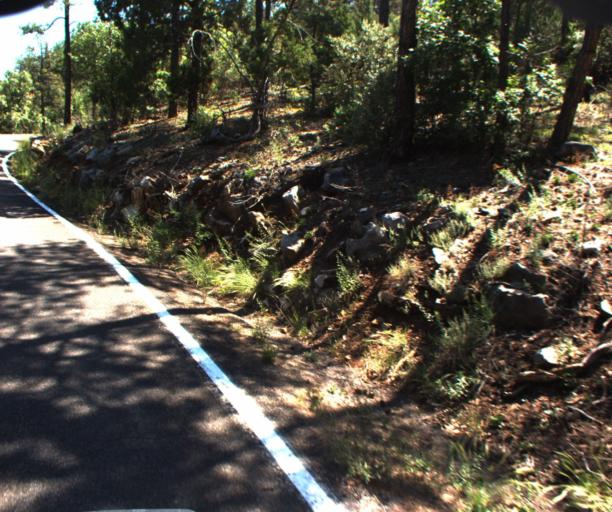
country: US
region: Arizona
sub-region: Greenlee County
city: Morenci
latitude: 33.2063
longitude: -109.3803
